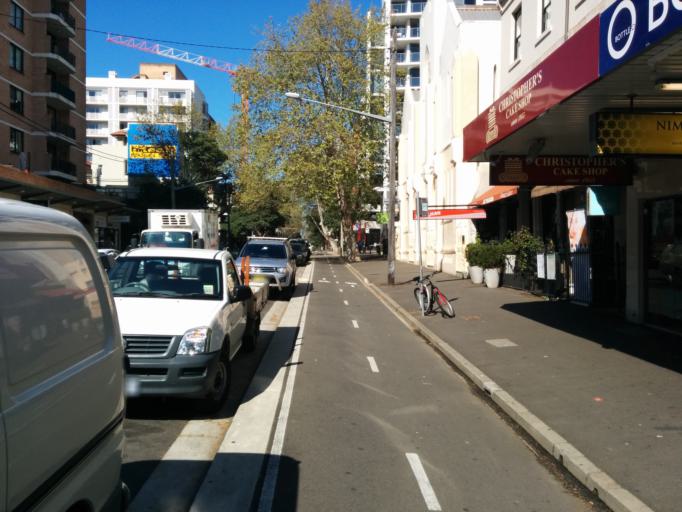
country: AU
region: New South Wales
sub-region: City of Sydney
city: Darlinghurst
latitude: -33.8815
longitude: 151.2166
